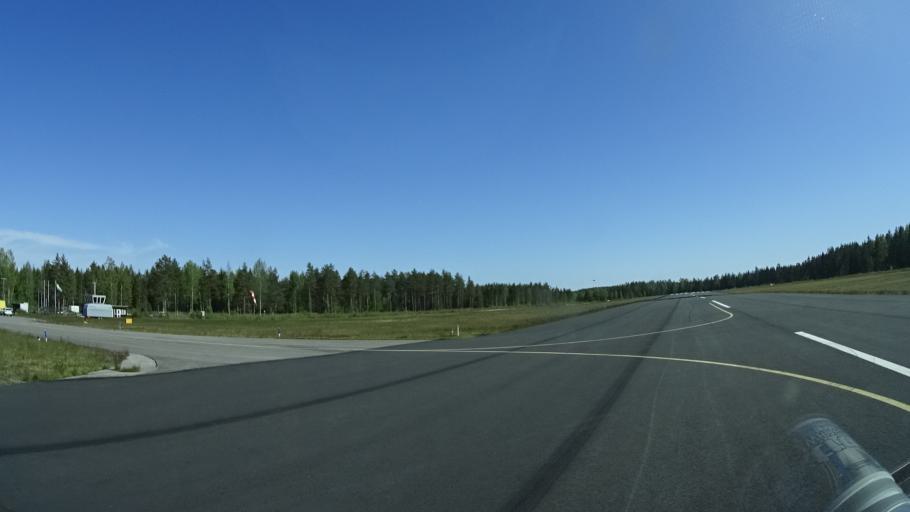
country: SE
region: Kalmar
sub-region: Vasterviks Kommun
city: Vaestervik
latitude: 57.7772
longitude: 16.5267
